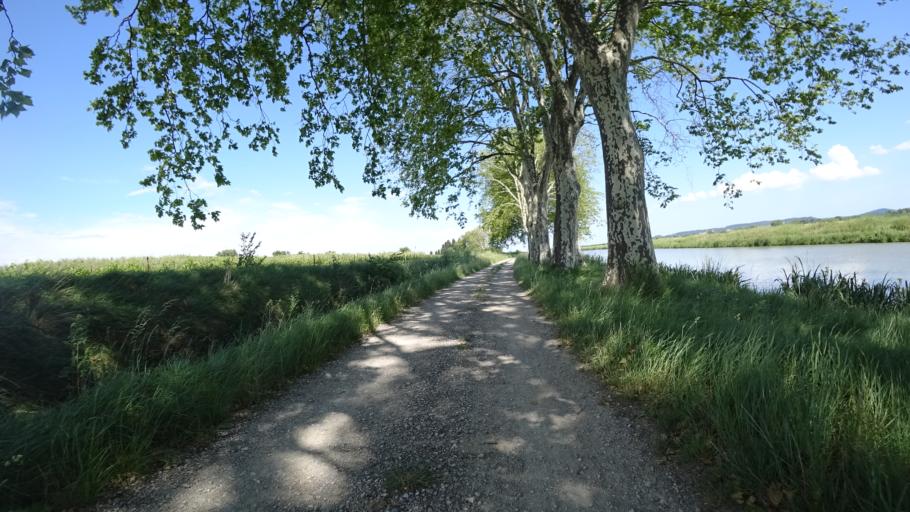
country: FR
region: Languedoc-Roussillon
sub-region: Departement de l'Aude
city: Ginestas
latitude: 43.2492
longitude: 2.8751
